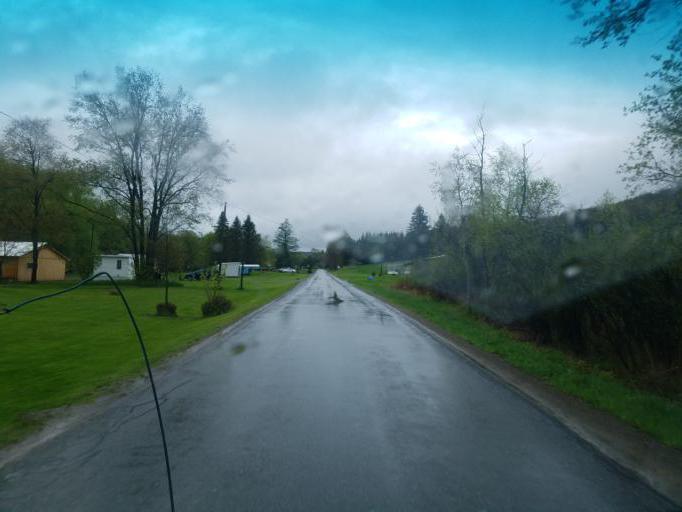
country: US
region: Pennsylvania
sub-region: Tioga County
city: Westfield
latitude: 41.9476
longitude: -77.6474
